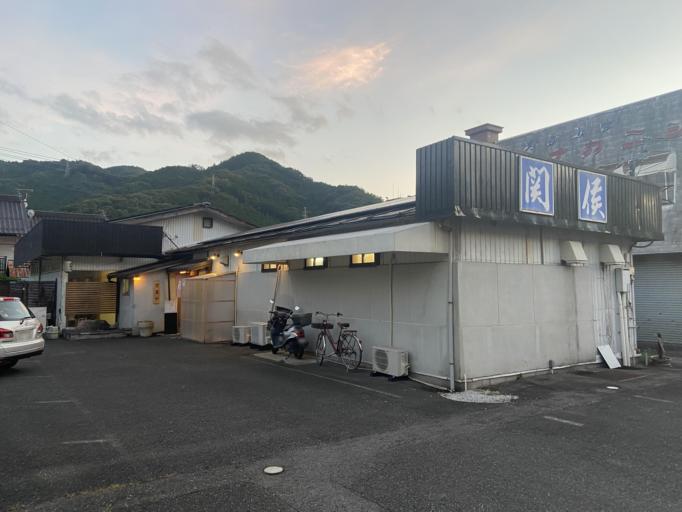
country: JP
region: Okayama
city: Niimi
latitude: 34.9893
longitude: 133.4589
